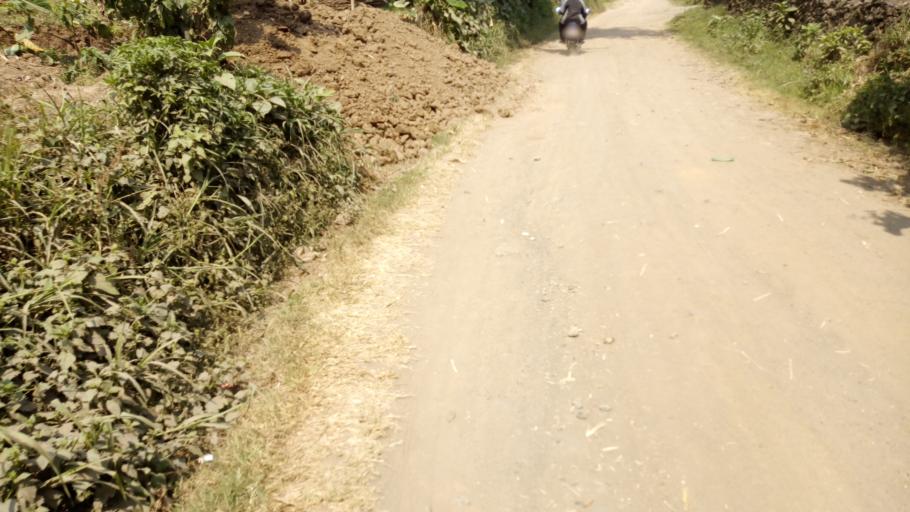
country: UG
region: Western Region
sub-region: Kisoro District
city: Kisoro
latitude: -1.3334
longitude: 29.7632
